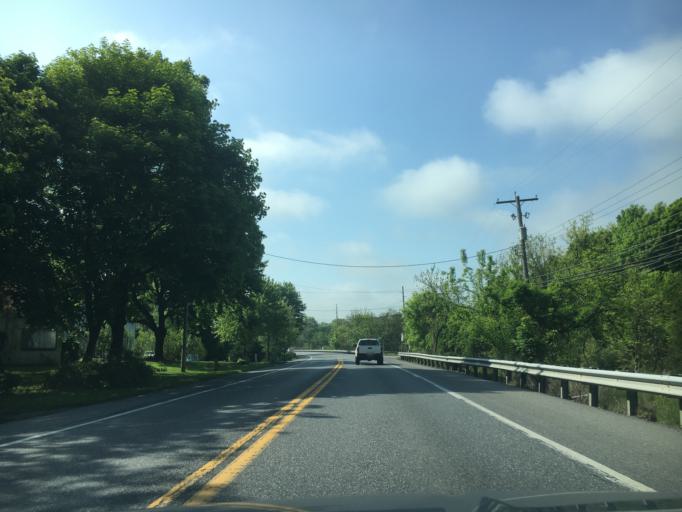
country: US
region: Pennsylvania
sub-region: Berks County
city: Boyertown
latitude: 40.3411
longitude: -75.6588
